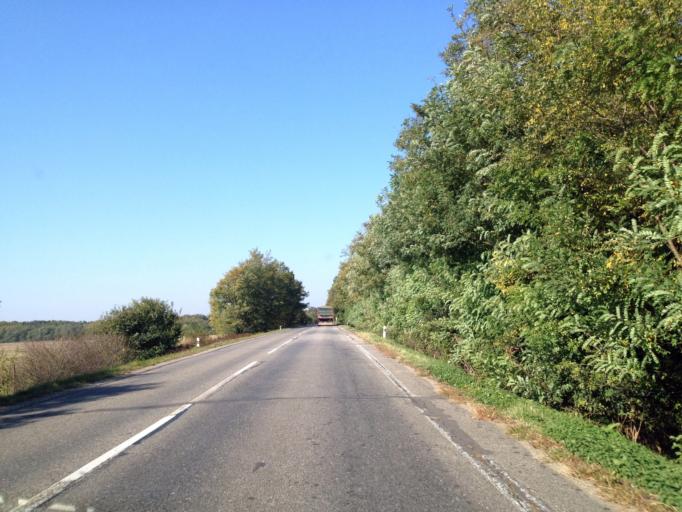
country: SK
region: Nitriansky
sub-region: Okres Komarno
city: Hurbanovo
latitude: 47.9256
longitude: 18.2249
